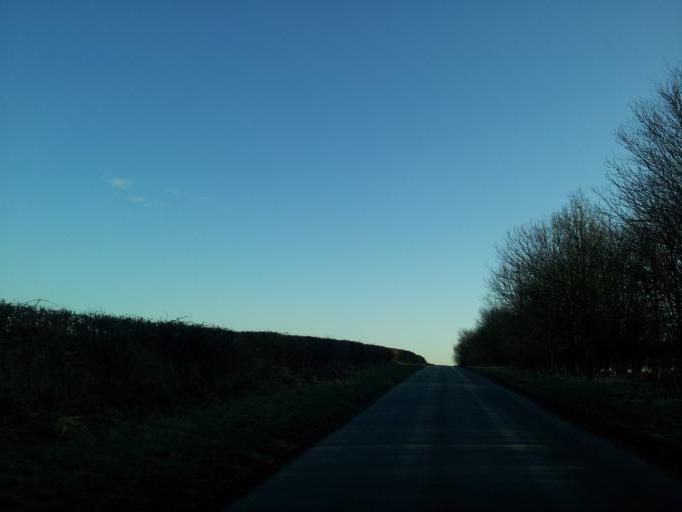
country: GB
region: England
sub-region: Lincolnshire
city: Horncastle
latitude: 53.2550
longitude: -0.1089
